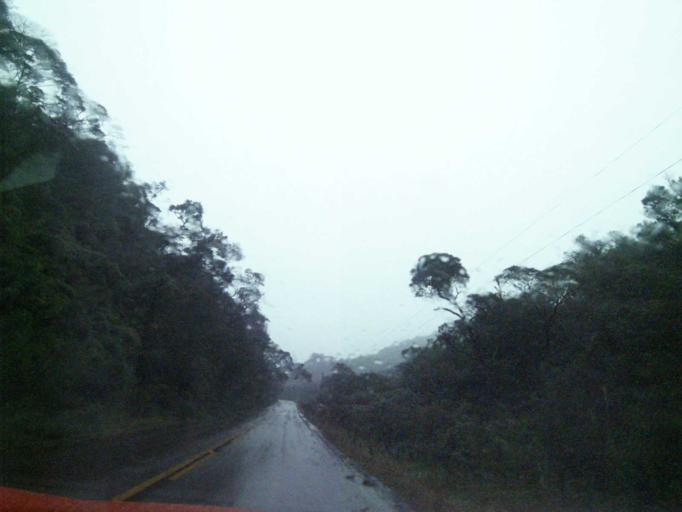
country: BR
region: Santa Catarina
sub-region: Anitapolis
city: Anitapolis
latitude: -27.7500
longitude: -49.0354
